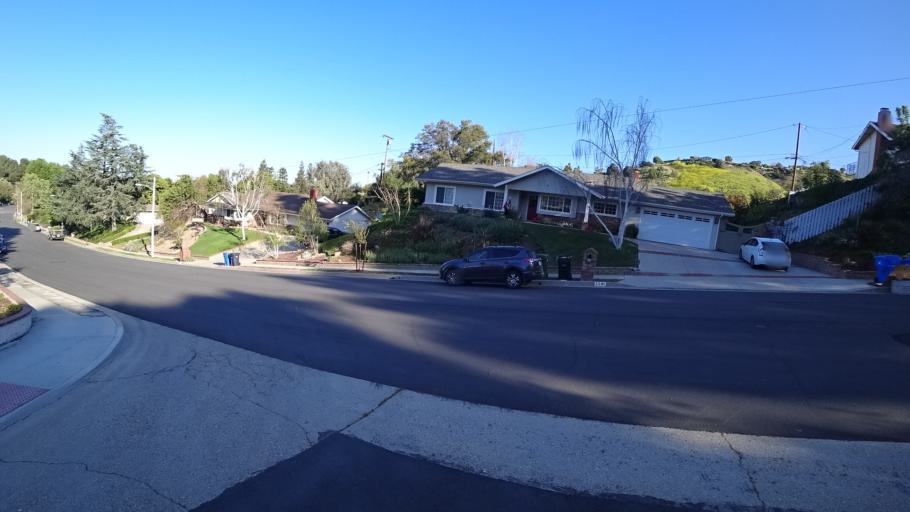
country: US
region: California
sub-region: Ventura County
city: Thousand Oaks
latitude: 34.1890
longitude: -118.8352
